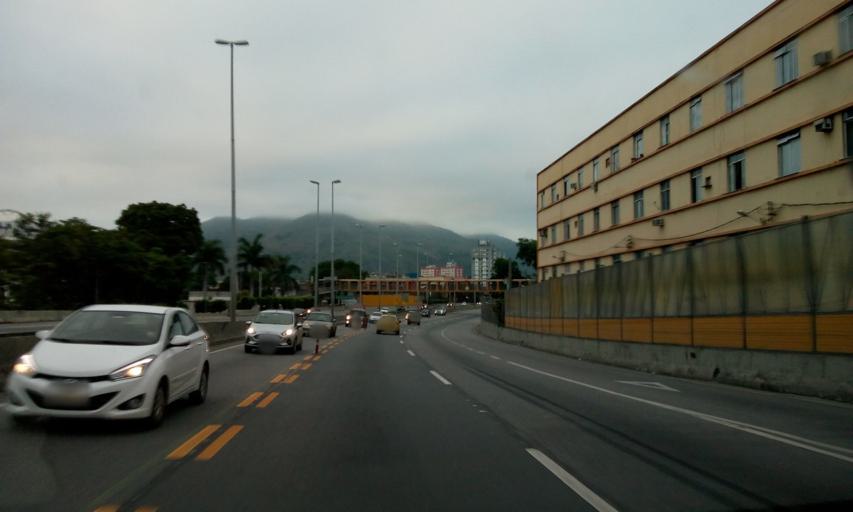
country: BR
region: Rio de Janeiro
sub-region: Rio De Janeiro
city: Rio de Janeiro
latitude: -22.8861
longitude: -43.2922
